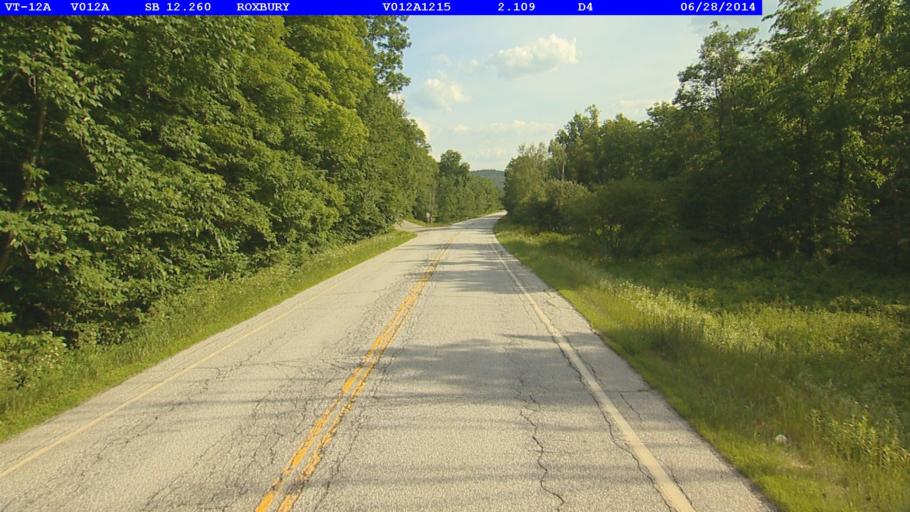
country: US
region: Vermont
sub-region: Washington County
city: Northfield
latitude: 44.0589
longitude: -72.7426
